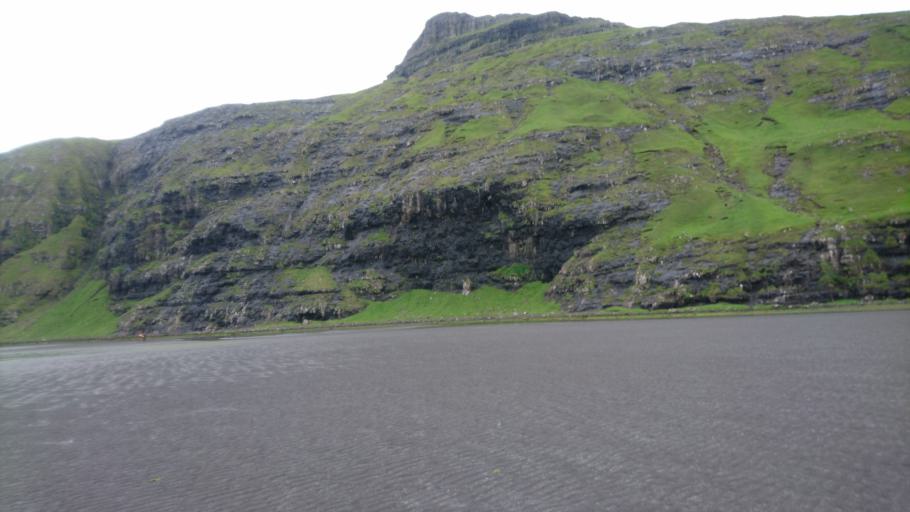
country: FO
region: Streymoy
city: Vestmanna
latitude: 62.2484
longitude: -7.1930
